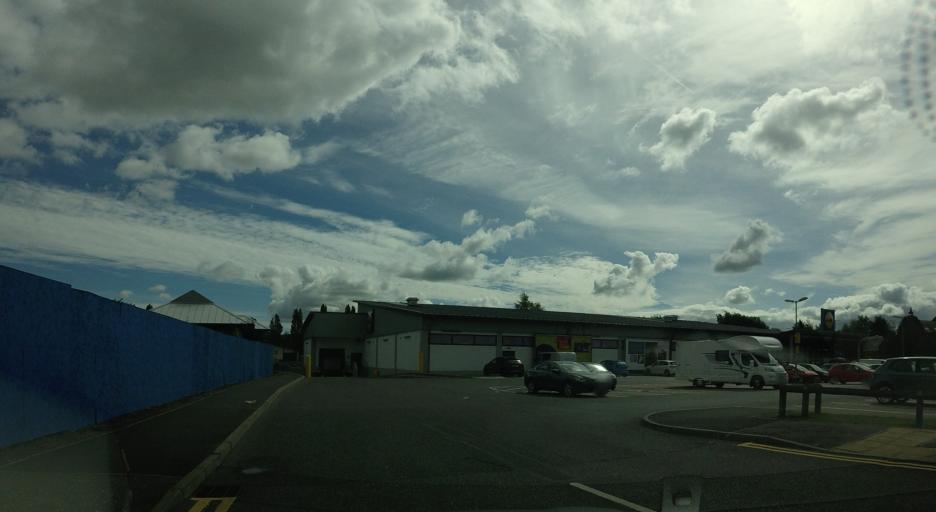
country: GB
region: Scotland
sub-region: Perth and Kinross
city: Perth
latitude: 56.3965
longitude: -3.4457
